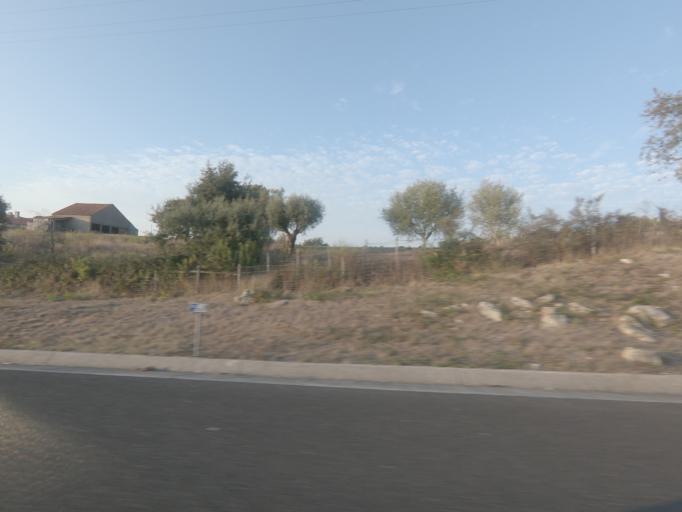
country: PT
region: Leiria
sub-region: Leiria
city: Santa Catarina da Serra
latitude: 39.7023
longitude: -8.6999
